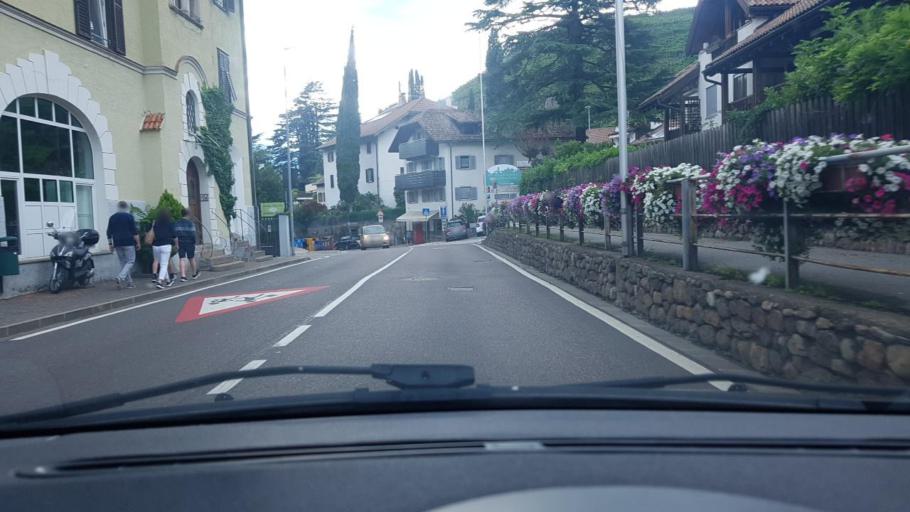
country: IT
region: Trentino-Alto Adige
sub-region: Bolzano
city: Cardano
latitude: 46.4987
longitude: 11.3757
